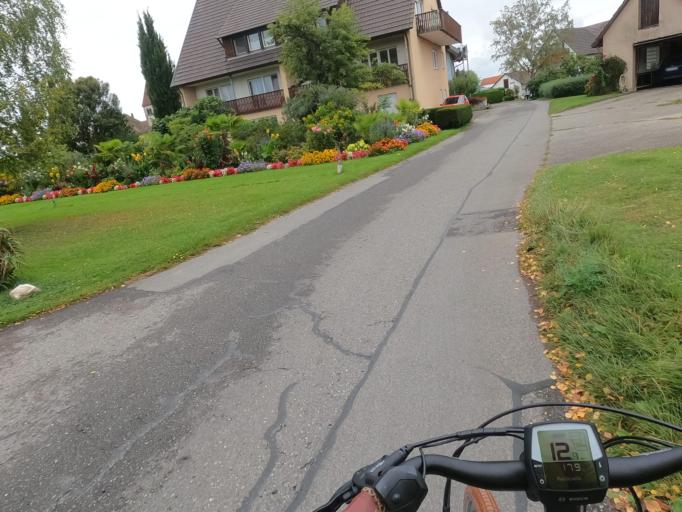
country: DE
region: Baden-Wuerttemberg
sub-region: Freiburg Region
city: Reichenau
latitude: 47.7056
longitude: 9.0462
